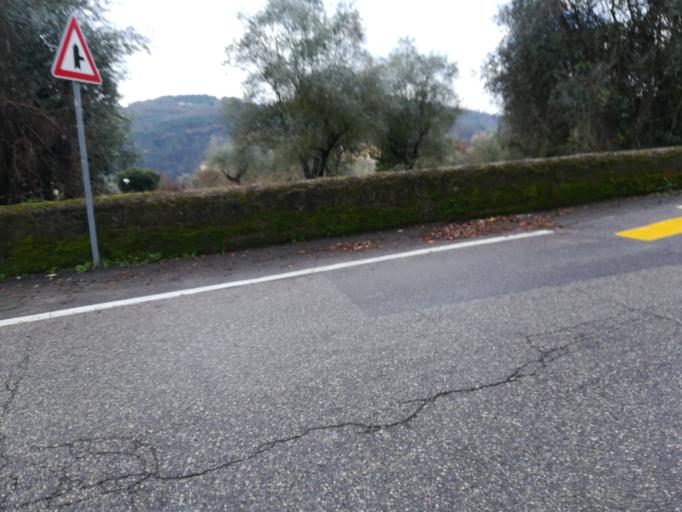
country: IT
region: Tuscany
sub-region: Provincia di Prato
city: Comeana
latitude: 43.7961
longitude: 11.0505
